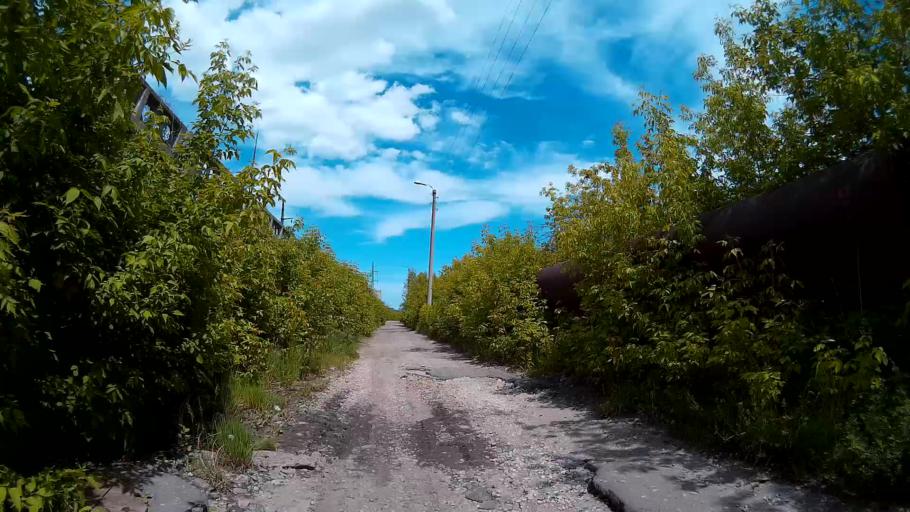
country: RU
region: Ulyanovsk
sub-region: Ulyanovskiy Rayon
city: Ulyanovsk
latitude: 54.2826
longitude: 48.3633
